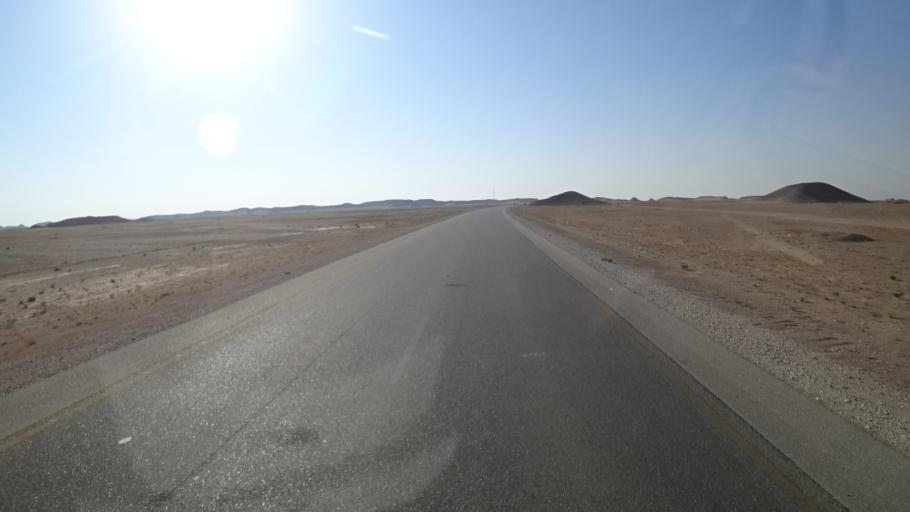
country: OM
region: Zufar
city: Salalah
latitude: 17.6393
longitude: 53.8753
